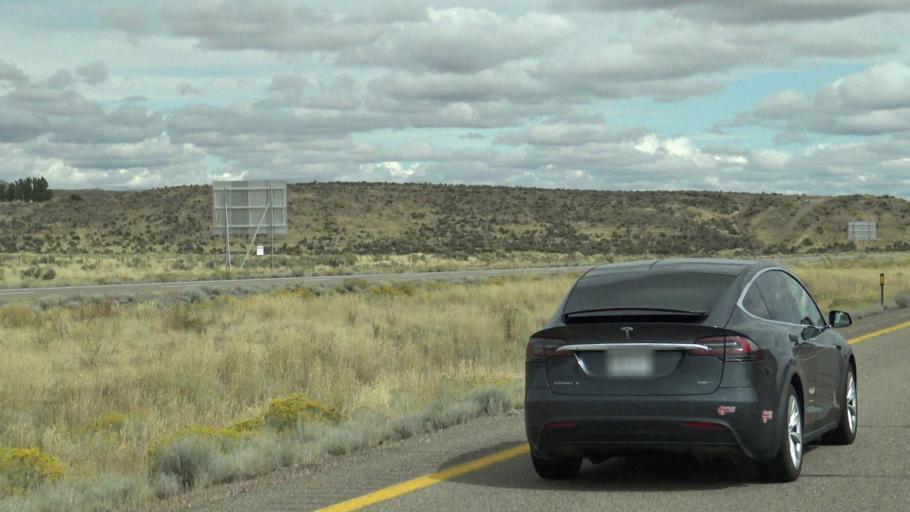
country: US
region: Nevada
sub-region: Elko County
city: Elko
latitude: 40.8696
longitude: -115.7284
